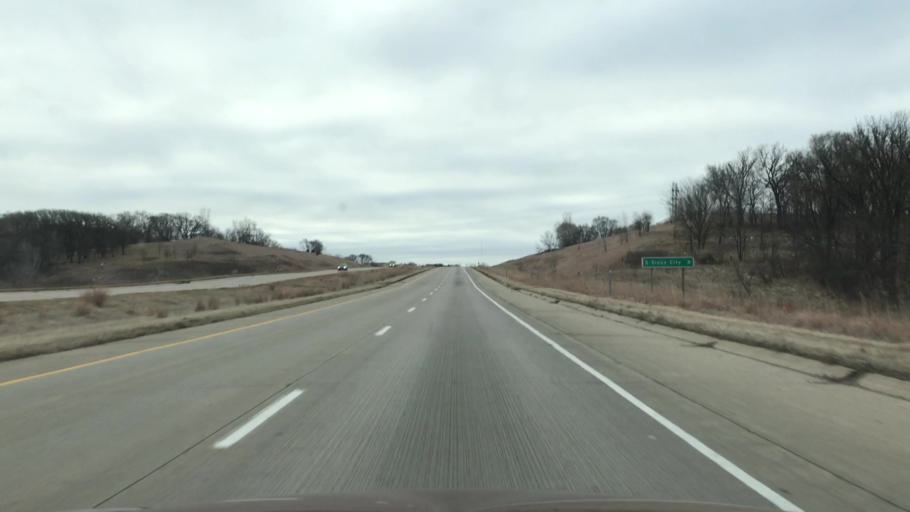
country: US
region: Iowa
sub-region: Woodbury County
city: Sioux City
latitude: 42.5069
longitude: -96.3273
